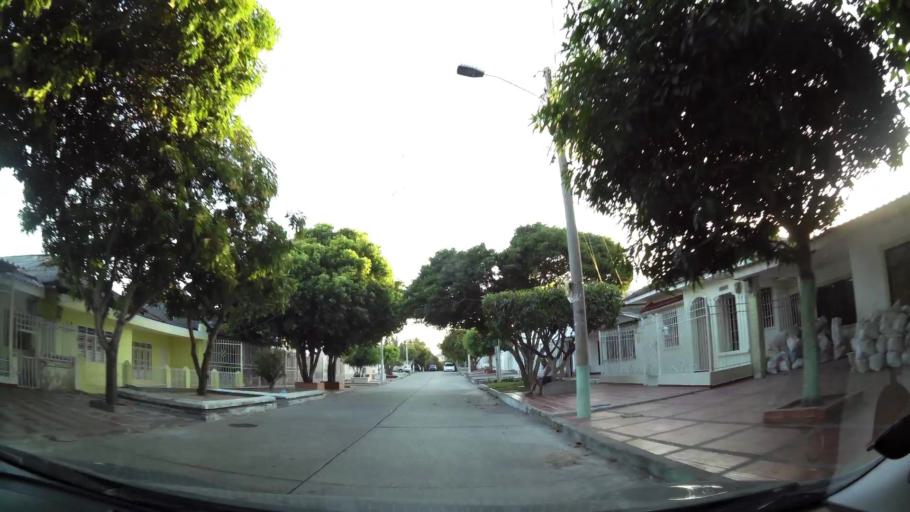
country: CO
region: Atlantico
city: Barranquilla
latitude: 10.9779
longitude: -74.8027
